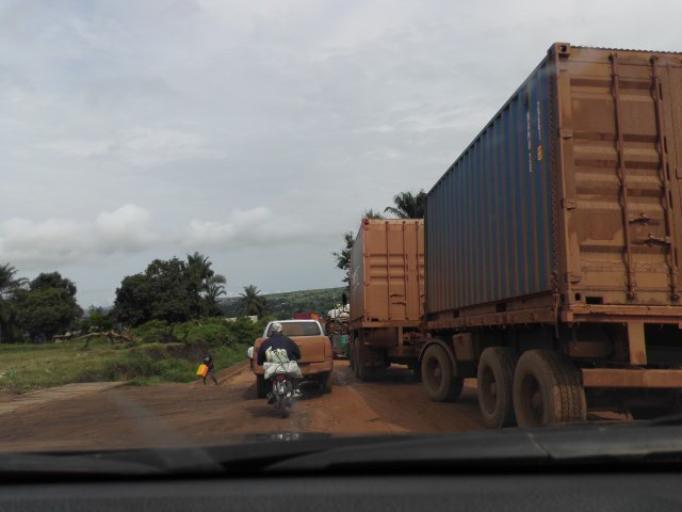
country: CD
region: Eastern Province
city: Bunia
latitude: 1.3661
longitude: 29.7641
